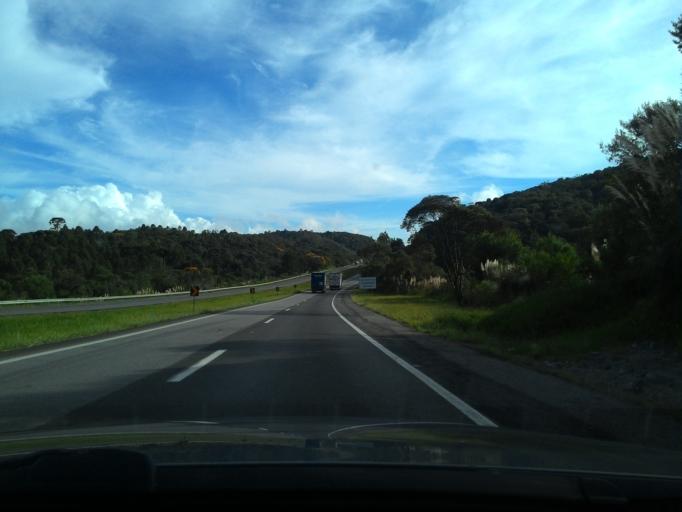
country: BR
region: Parana
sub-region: Campina Grande Do Sul
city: Campina Grande do Sul
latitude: -25.2625
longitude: -48.9148
